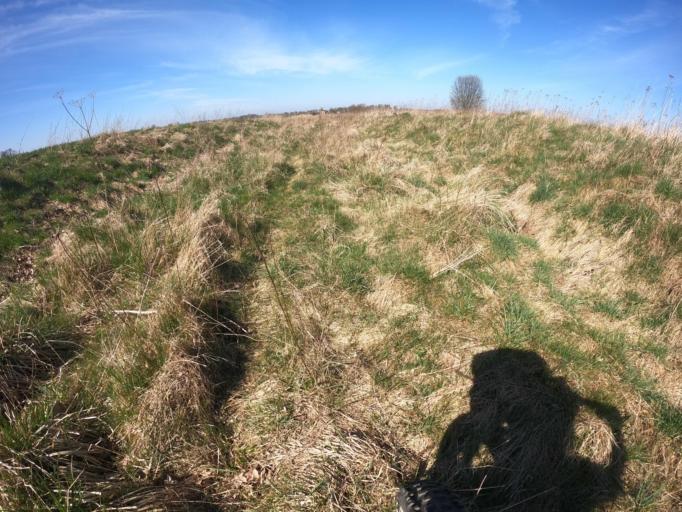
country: PL
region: West Pomeranian Voivodeship
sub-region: Powiat gryficki
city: Brojce
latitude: 53.9897
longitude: 15.3857
